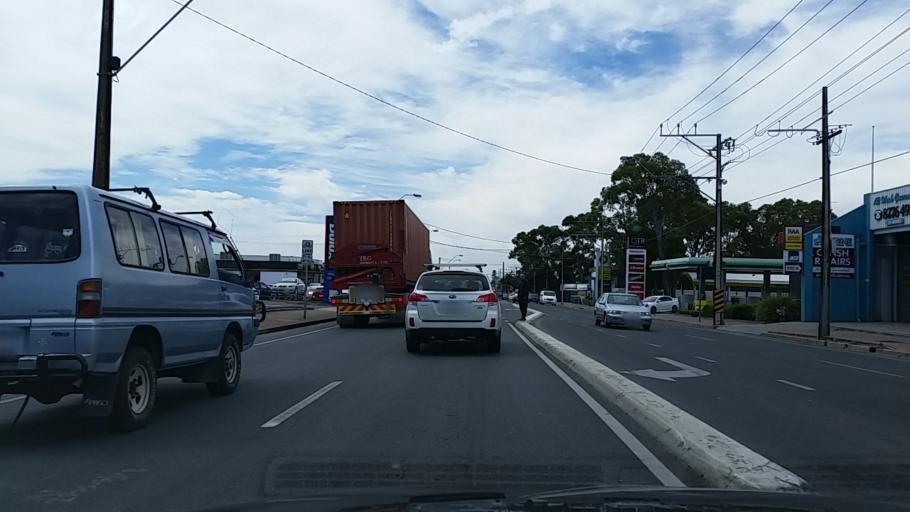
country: AU
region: South Australia
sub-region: Marion
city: Clovelly Park
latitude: -34.9984
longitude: 138.5753
